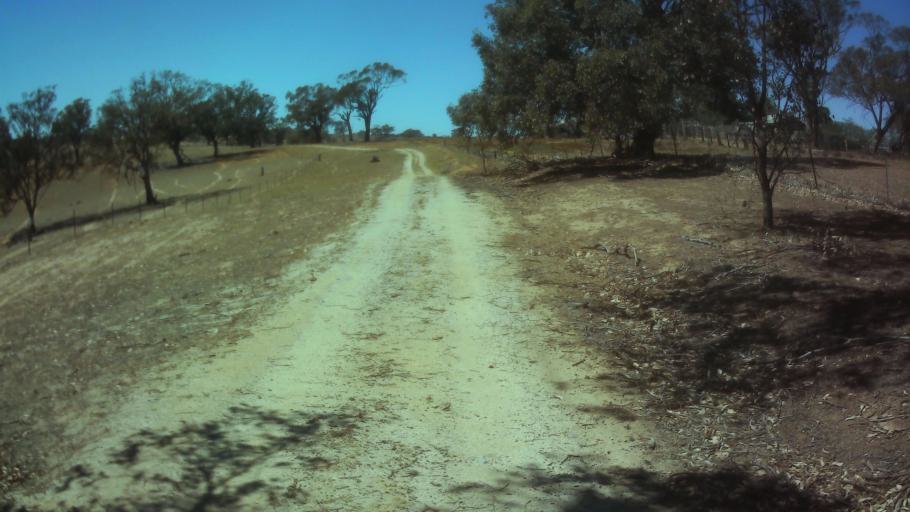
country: AU
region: New South Wales
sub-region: Cowra
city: Cowra
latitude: -33.8885
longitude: 148.4983
